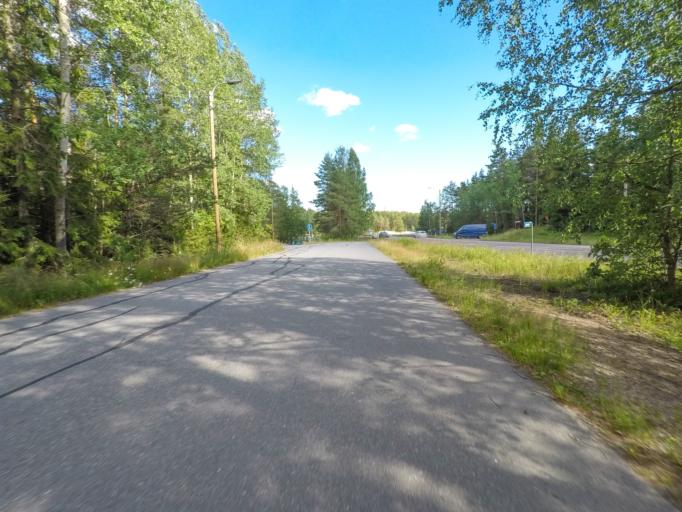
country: FI
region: South Karelia
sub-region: Lappeenranta
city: Lappeenranta
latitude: 61.1012
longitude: 28.1282
